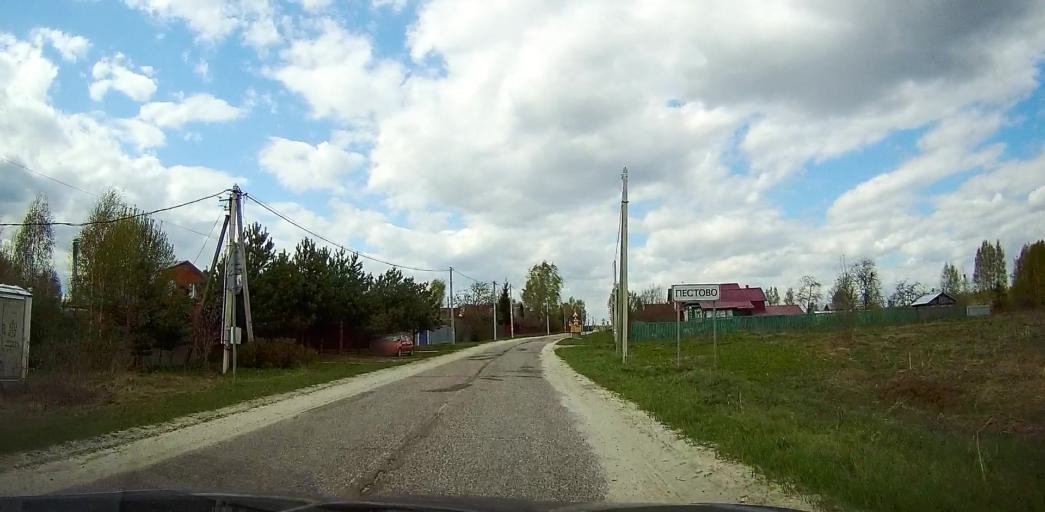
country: RU
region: Moskovskaya
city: Davydovo
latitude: 55.6359
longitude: 38.7820
